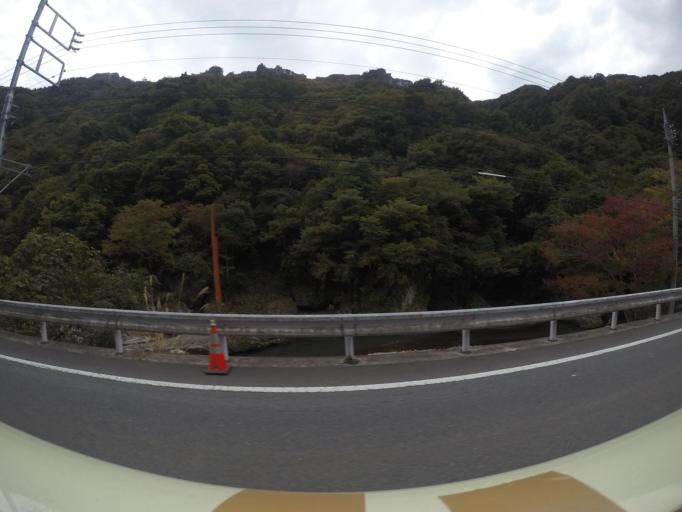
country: JP
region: Gunma
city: Tomioka
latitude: 36.0867
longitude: 138.8415
